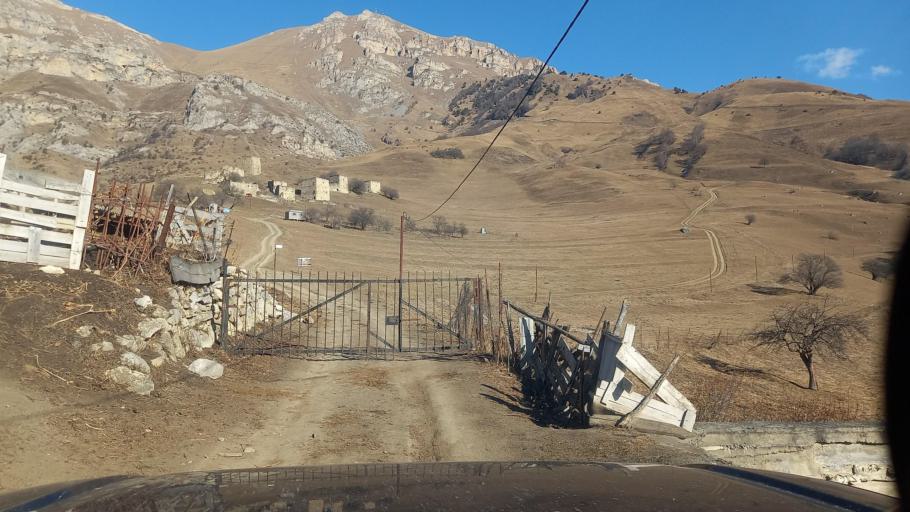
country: RU
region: Ingushetiya
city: Dzhayrakh
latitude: 42.8346
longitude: 44.7193
